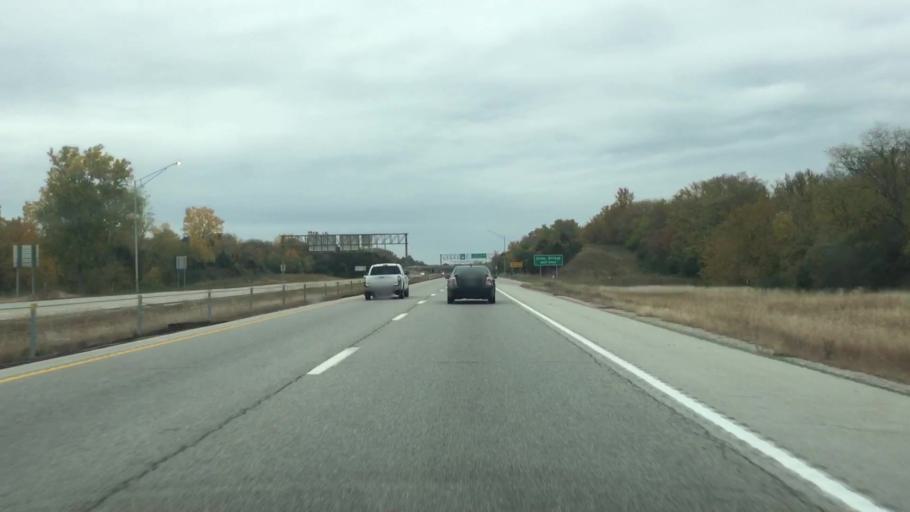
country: US
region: Missouri
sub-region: Jackson County
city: Lees Summit
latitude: 38.9368
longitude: -94.4069
